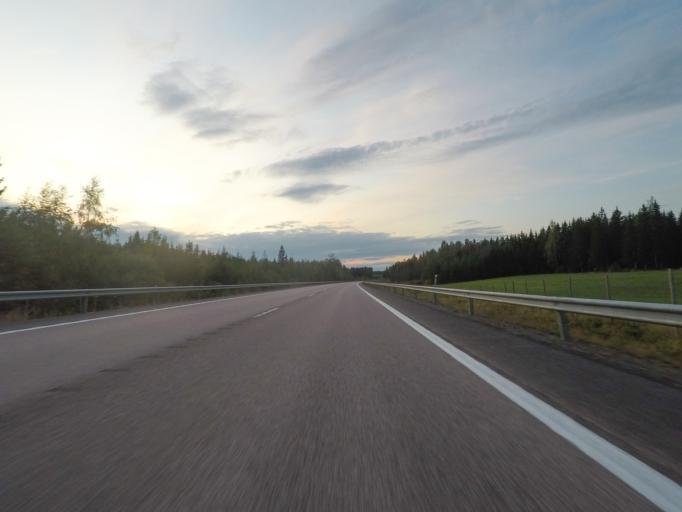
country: FI
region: Central Finland
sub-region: Jyvaeskylae
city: Saeynaetsalo
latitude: 62.1395
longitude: 25.9040
